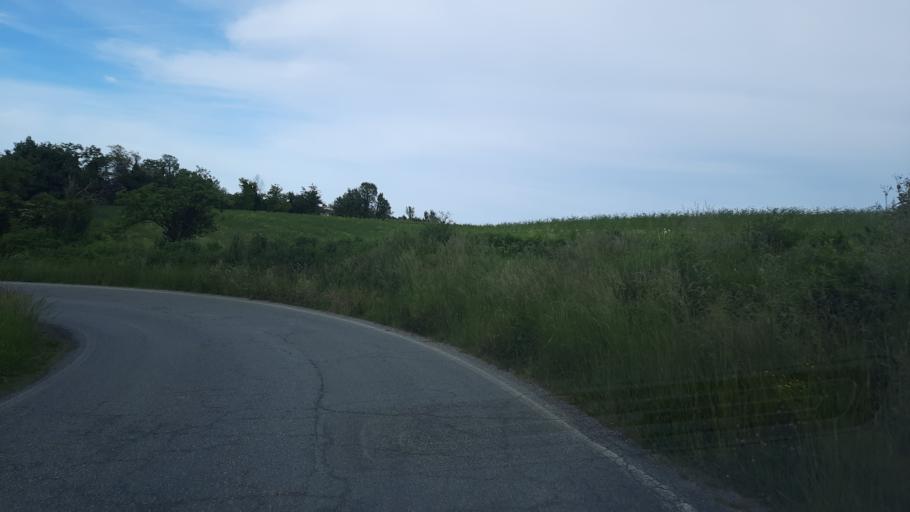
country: IT
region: Piedmont
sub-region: Provincia di Alessandria
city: Alfiano Natta
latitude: 45.0449
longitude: 8.2210
